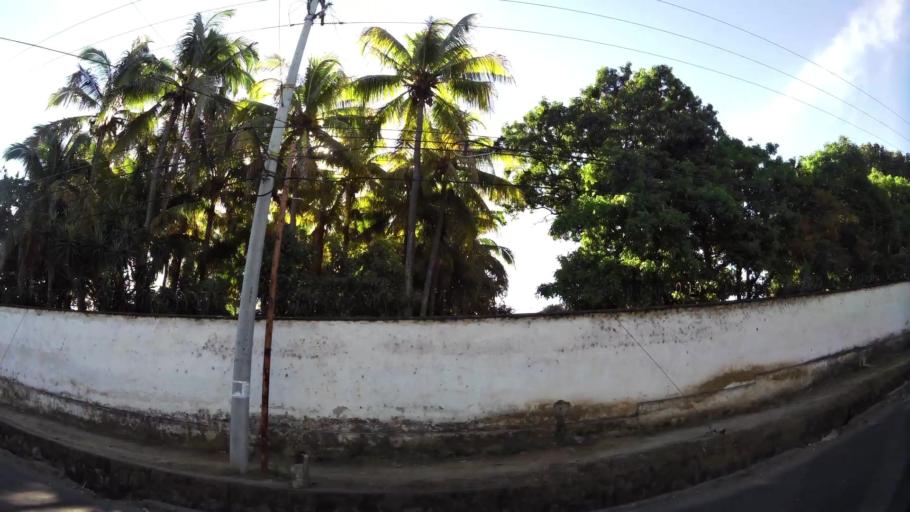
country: SV
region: Santa Ana
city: Santa Ana
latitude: 13.9876
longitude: -89.5666
